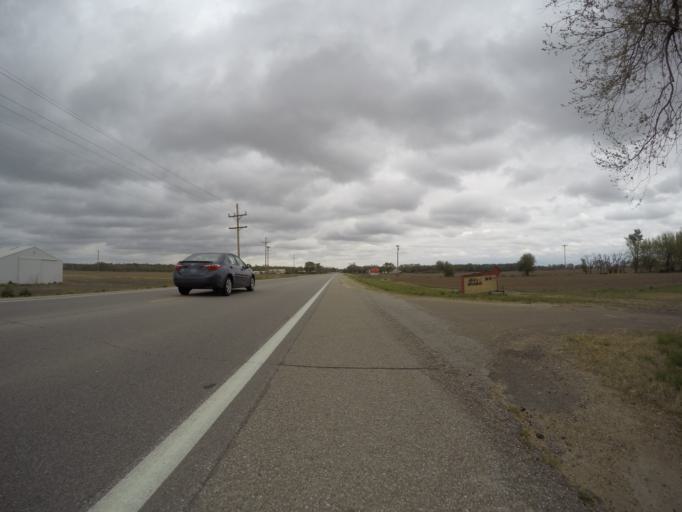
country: US
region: Kansas
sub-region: Pottawatomie County
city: Wamego
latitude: 39.1877
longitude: -96.3052
